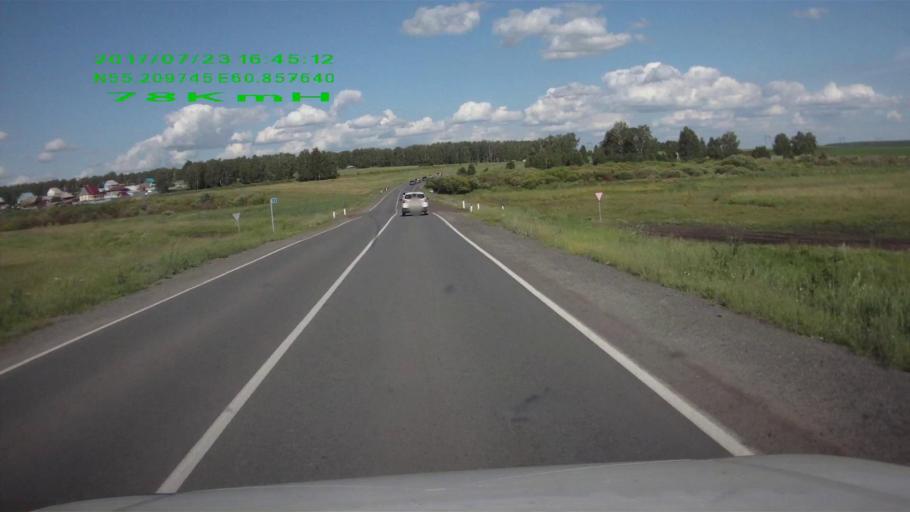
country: RU
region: Chelyabinsk
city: Argayash
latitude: 55.2097
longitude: 60.8576
